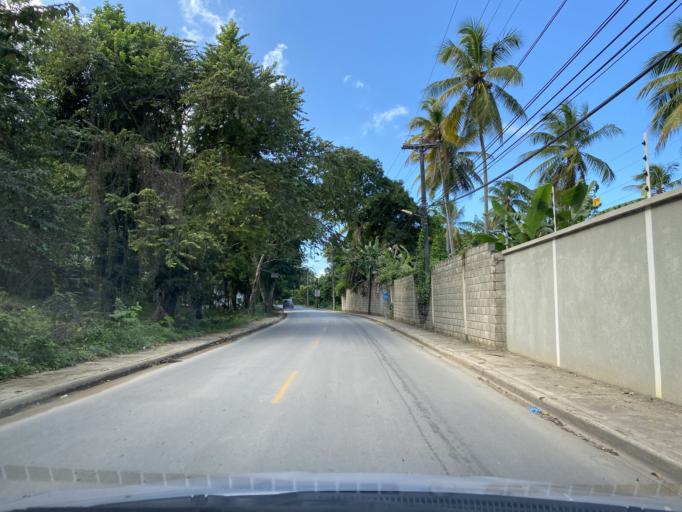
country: DO
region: Samana
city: Las Terrenas
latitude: 19.3063
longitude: -69.5573
